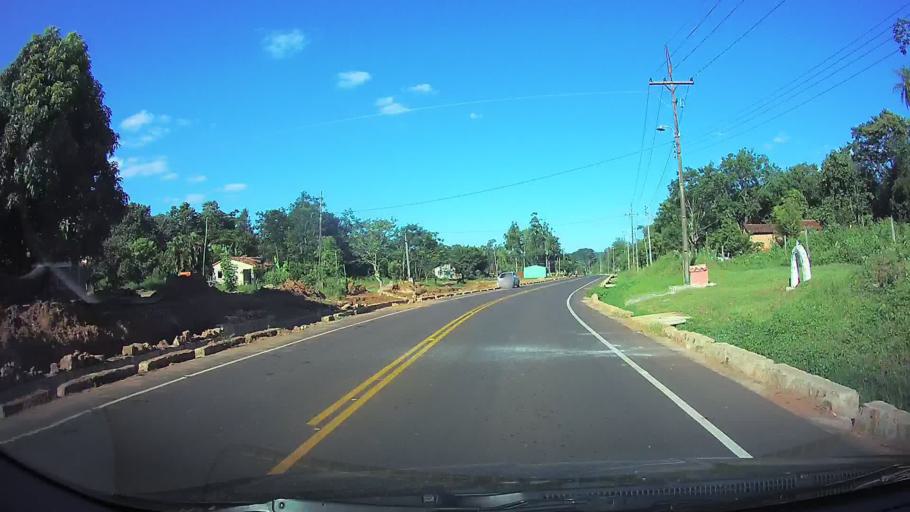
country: PY
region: Cordillera
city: Caacupe
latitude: -25.3252
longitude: -57.1570
